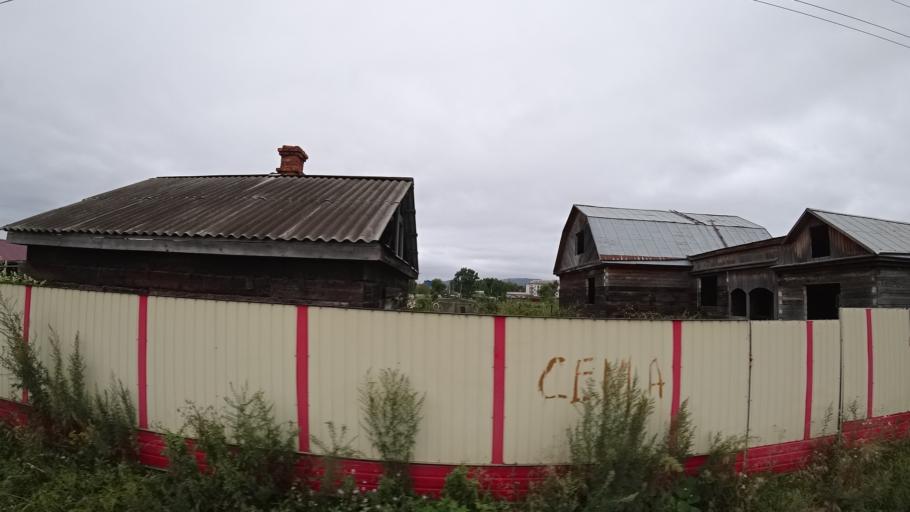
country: RU
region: Primorskiy
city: Chernigovka
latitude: 44.3363
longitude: 132.5345
